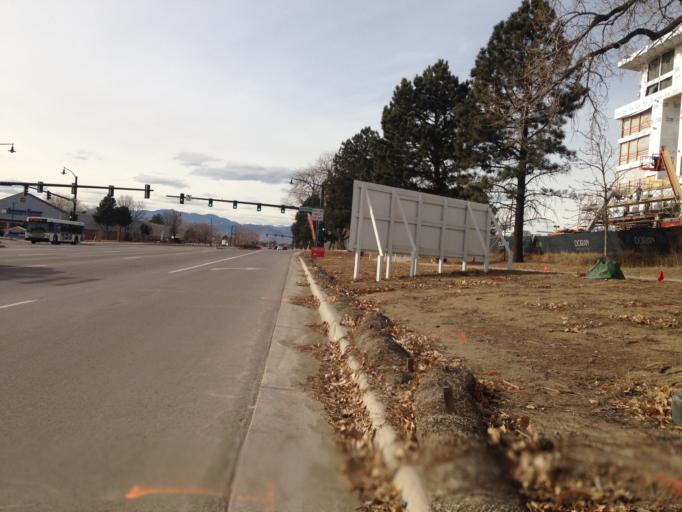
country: US
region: Colorado
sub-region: Adams County
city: Westminster
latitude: 39.8566
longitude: -105.0597
